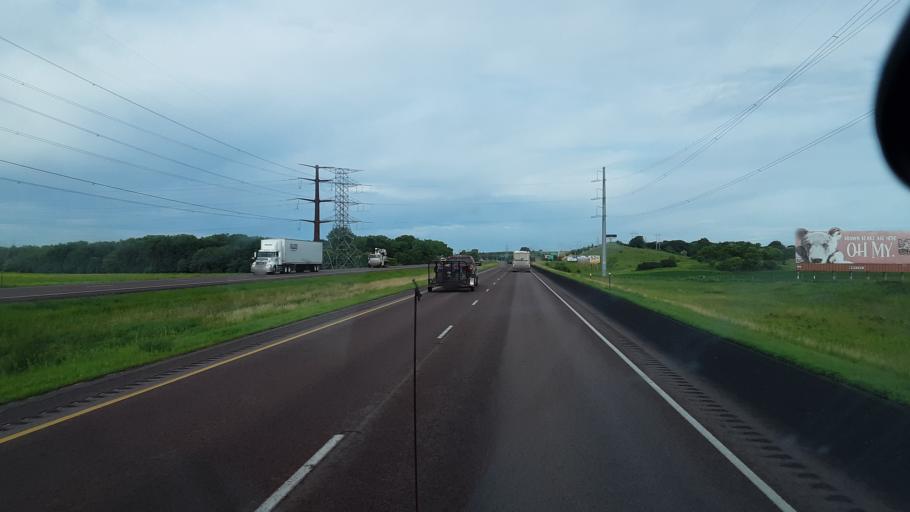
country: US
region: South Dakota
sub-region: Minnehaha County
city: Brandon
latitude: 43.6105
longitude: -96.6267
